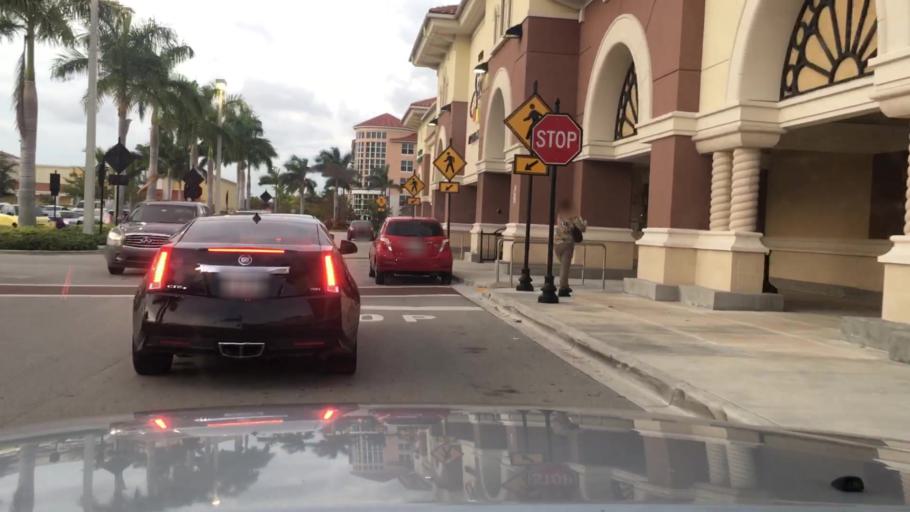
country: US
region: Florida
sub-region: Miami-Dade County
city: Fountainebleau
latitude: 25.7699
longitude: -80.3580
